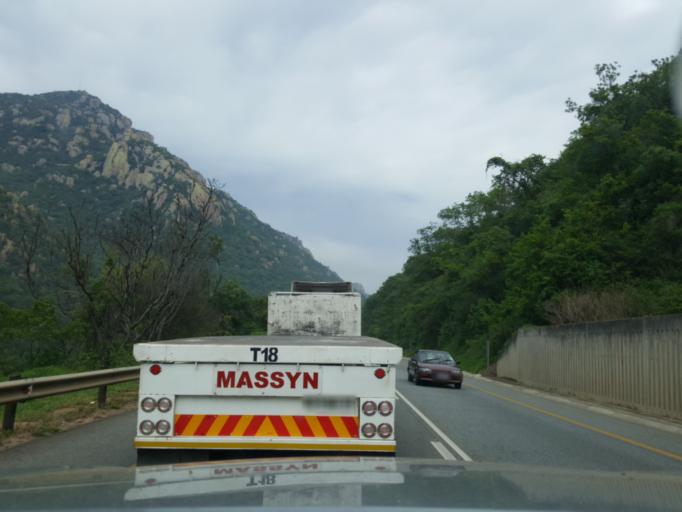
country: ZA
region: Mpumalanga
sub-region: Ehlanzeni District
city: Nelspruit
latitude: -25.5186
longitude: 31.2395
